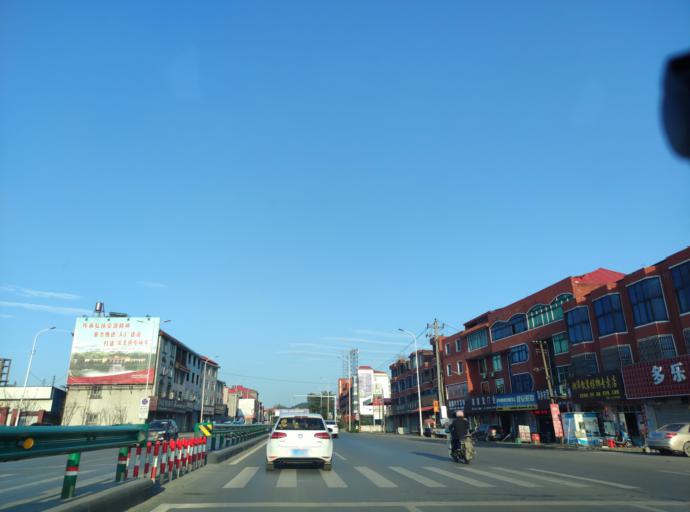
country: CN
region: Jiangxi Sheng
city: Xiangdong
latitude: 27.6489
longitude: 113.7747
